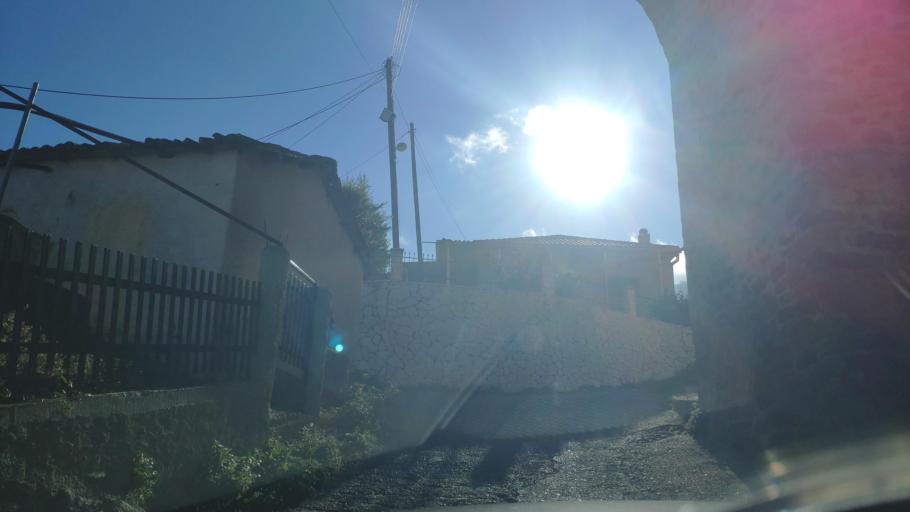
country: GR
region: West Greece
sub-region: Nomos Achaias
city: Aiyira
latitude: 38.0881
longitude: 22.4394
